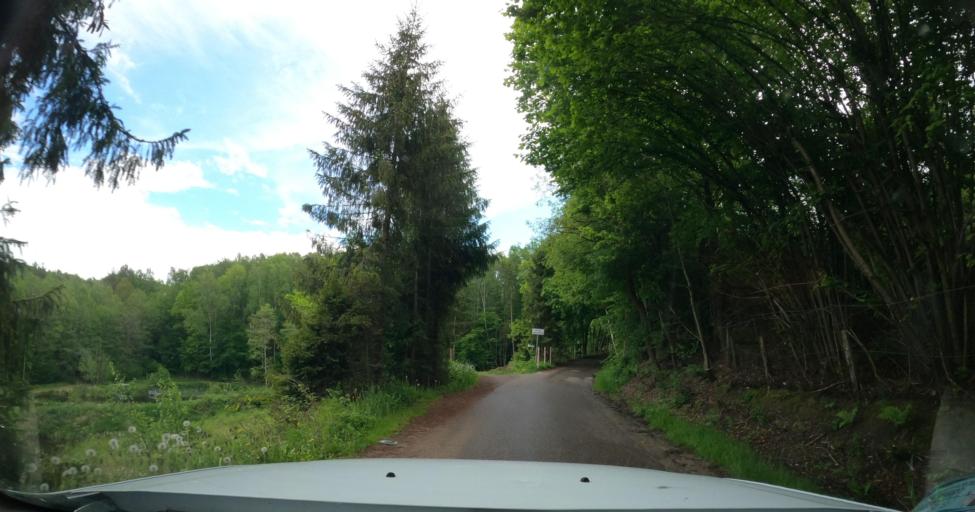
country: PL
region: Pomeranian Voivodeship
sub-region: Powiat kartuski
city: Garcz
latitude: 54.3325
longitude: 18.1402
